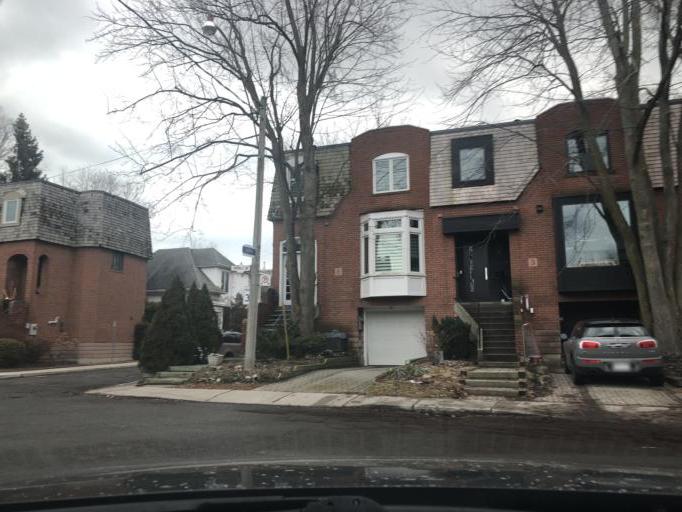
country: CA
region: Ontario
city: Toronto
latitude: 43.6789
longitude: -79.3356
